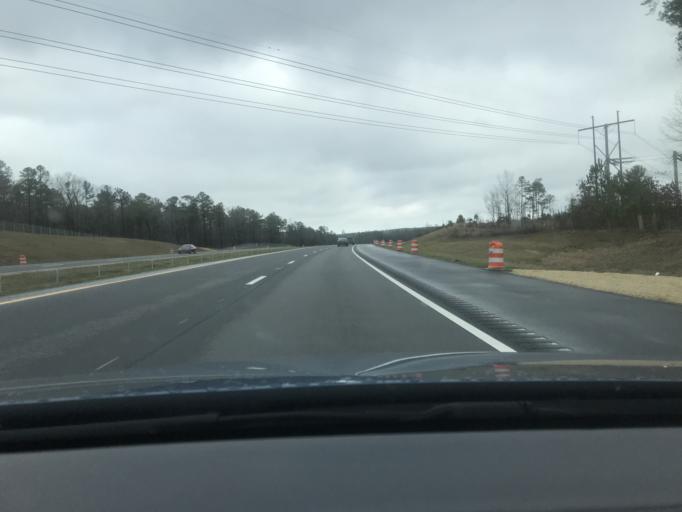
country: US
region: North Carolina
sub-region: Cumberland County
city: Fort Bragg
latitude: 35.0936
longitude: -79.0261
